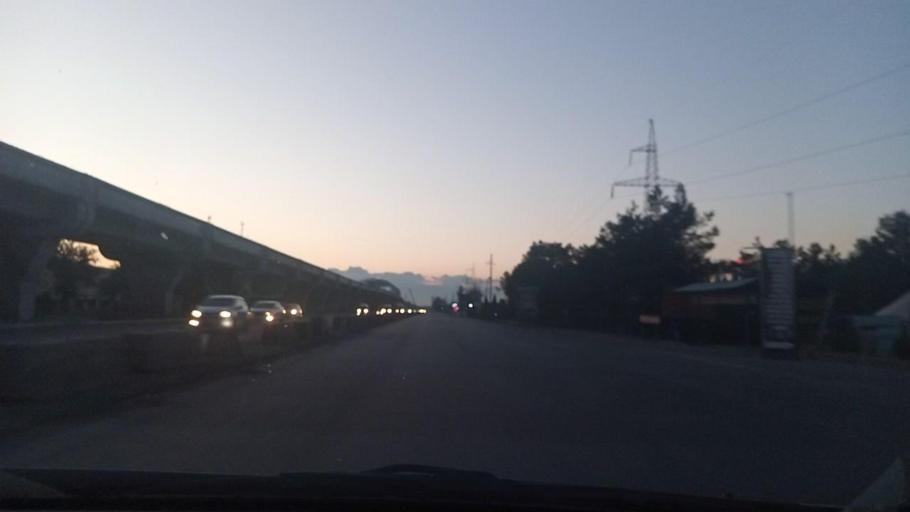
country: UZ
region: Toshkent Shahri
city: Bektemir
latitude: 41.2442
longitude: 69.2946
